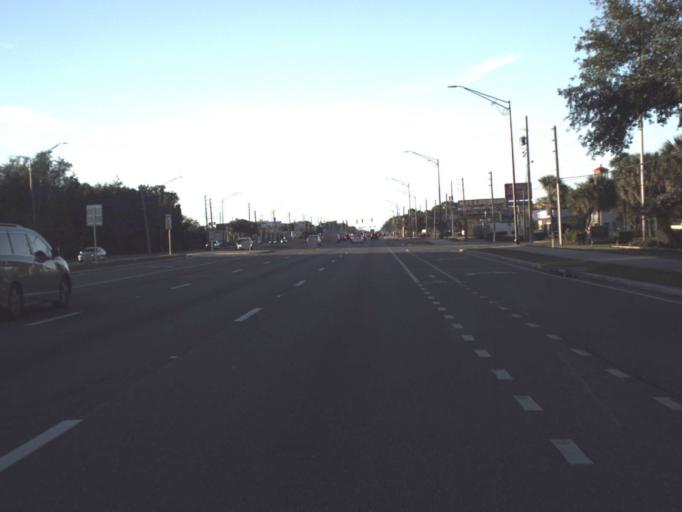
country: US
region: Florida
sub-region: Orange County
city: Conway
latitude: 28.4923
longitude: -81.3101
